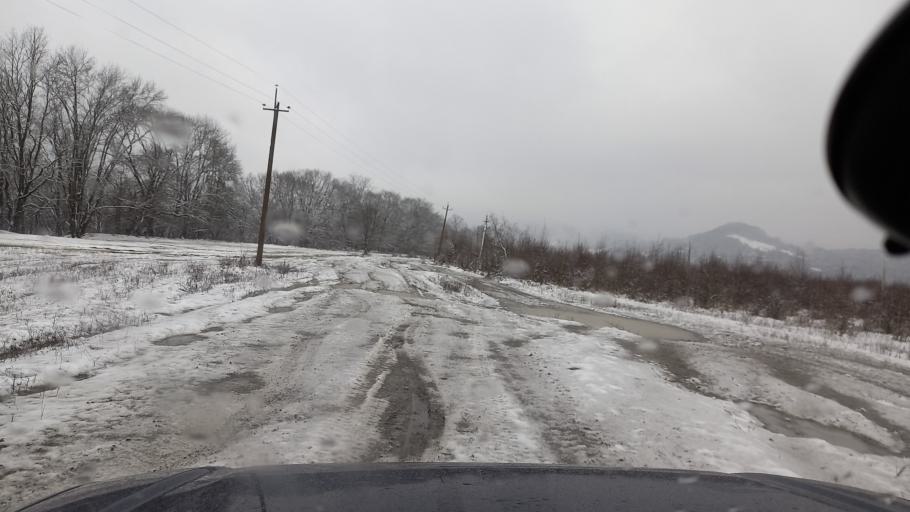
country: RU
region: Adygeya
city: Kamennomostskiy
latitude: 44.2180
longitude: 40.1773
